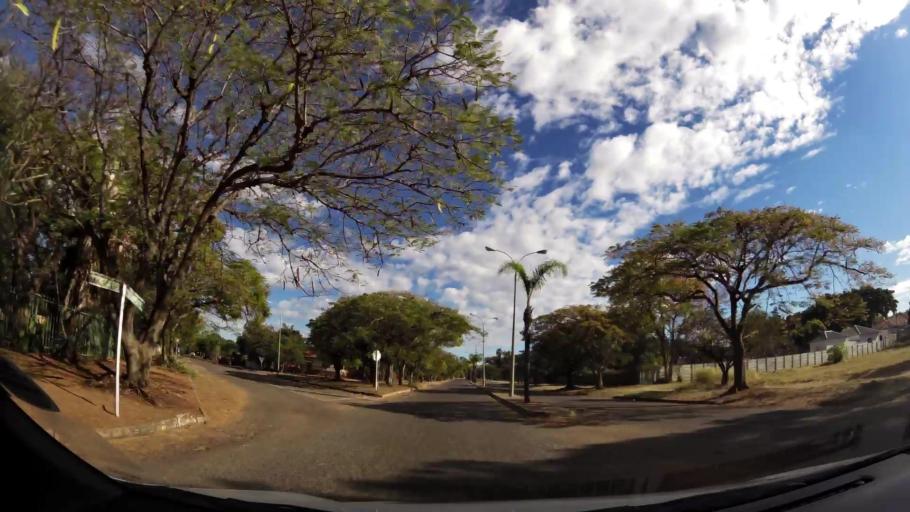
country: ZA
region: Limpopo
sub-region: Waterberg District Municipality
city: Warmbaths
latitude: -24.8847
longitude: 28.2830
